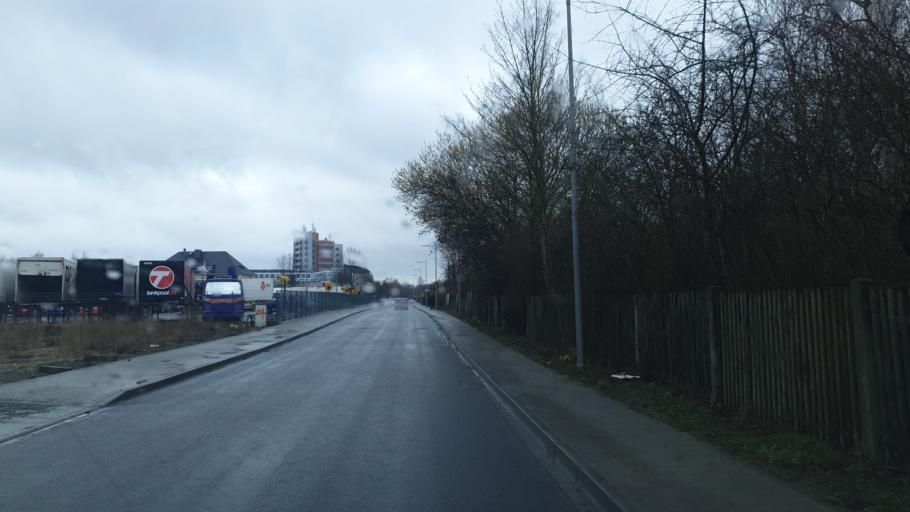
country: DE
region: Saxony
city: Taucha
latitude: 51.3394
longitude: 12.4703
